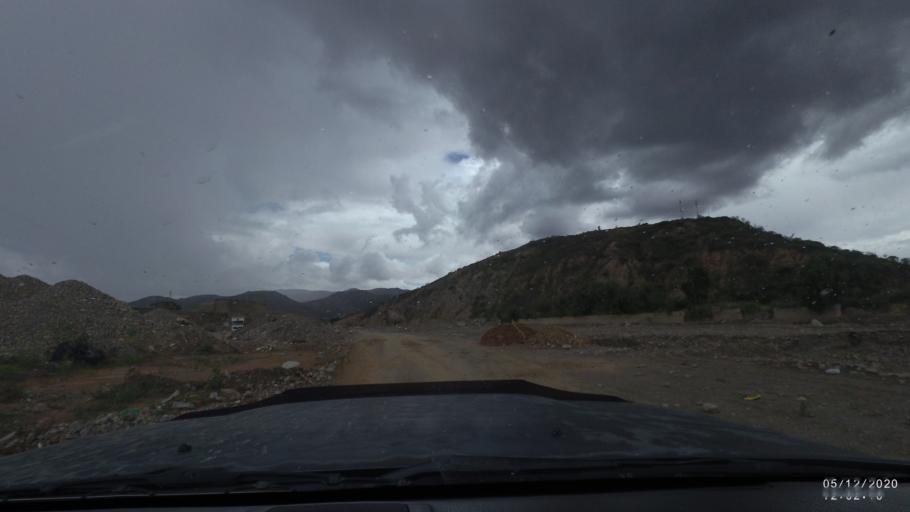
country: BO
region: Cochabamba
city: Sipe Sipe
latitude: -17.5752
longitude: -66.3502
